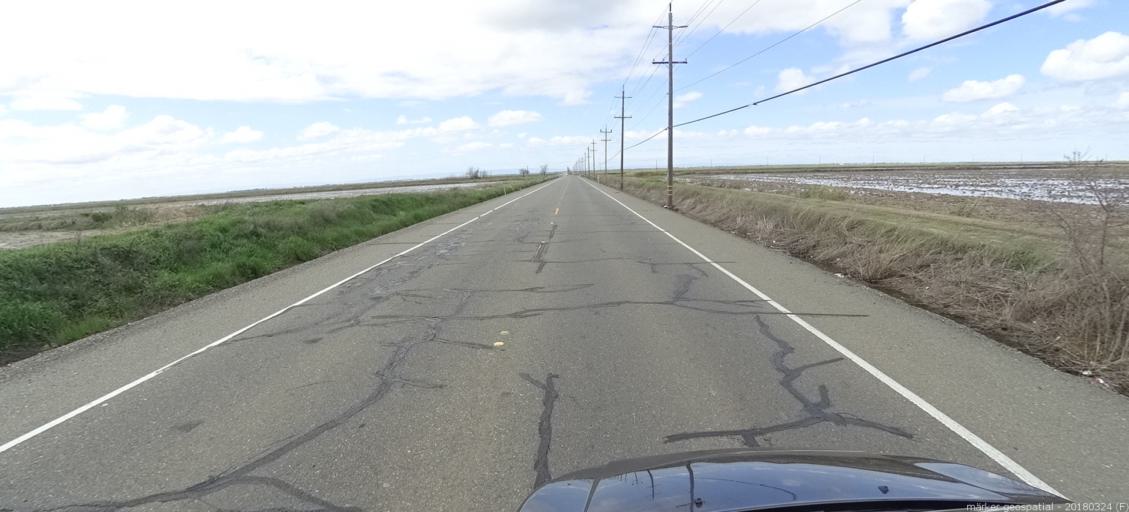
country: US
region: California
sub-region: Sacramento County
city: Elverta
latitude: 38.7146
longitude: -121.4963
